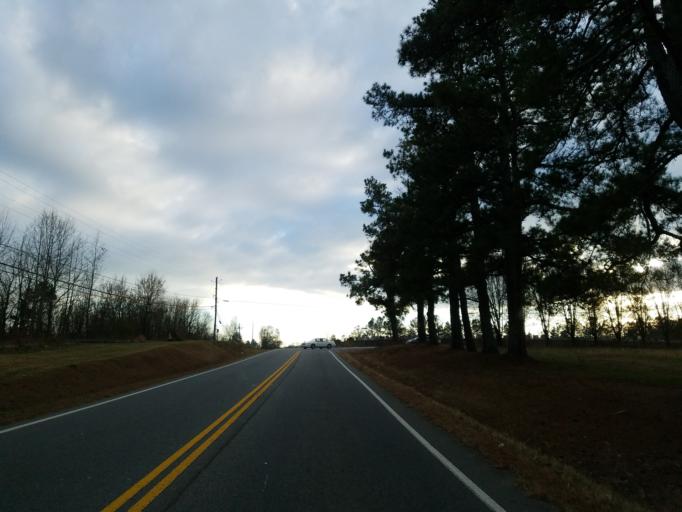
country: US
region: Georgia
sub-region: Forsyth County
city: Cumming
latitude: 34.2760
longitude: -84.0990
